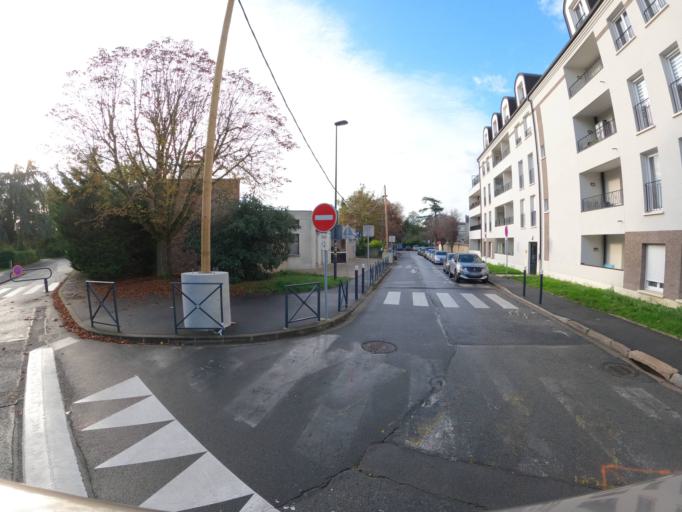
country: FR
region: Ile-de-France
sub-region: Departement de Seine-et-Marne
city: Brou-sur-Chantereine
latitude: 48.8835
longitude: 2.6307
